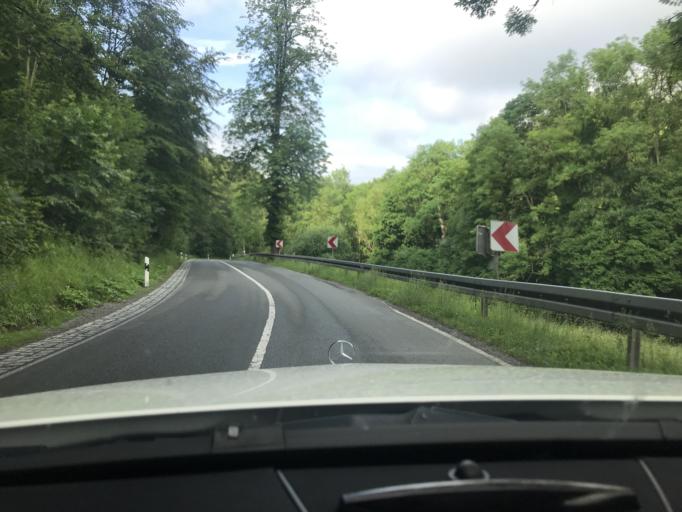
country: DE
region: Thuringia
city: Effelder
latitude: 51.2154
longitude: 10.2760
